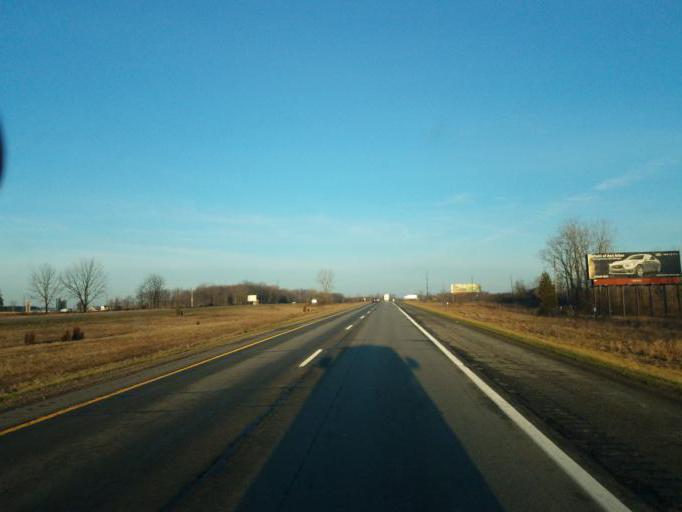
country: US
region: Michigan
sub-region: Livingston County
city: Fowlerville
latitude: 42.6467
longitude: -84.0859
